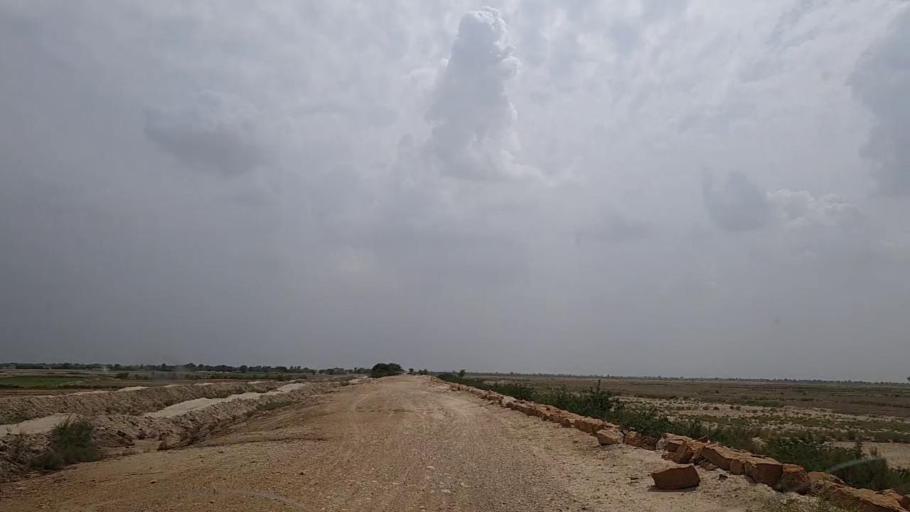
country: PK
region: Sindh
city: Johi
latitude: 26.7430
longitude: 67.5863
